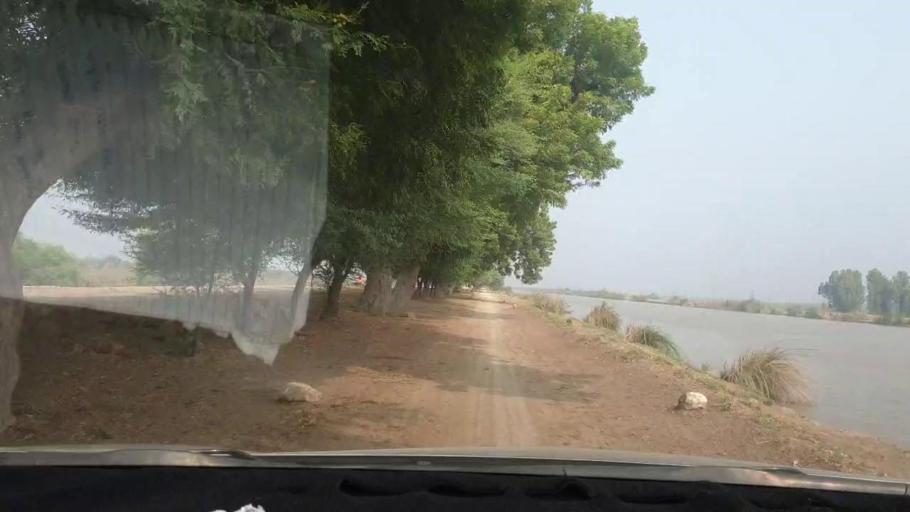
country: PK
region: Sindh
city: Matiari
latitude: 25.6744
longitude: 68.5577
